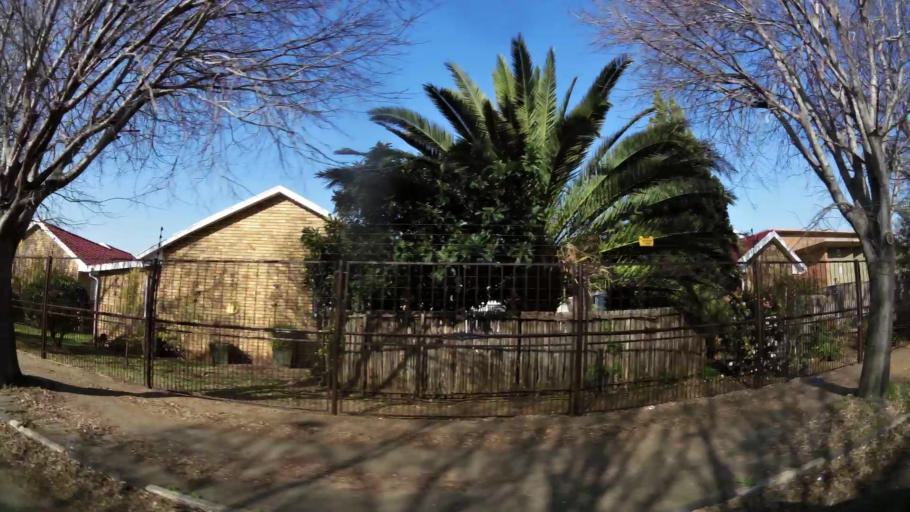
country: ZA
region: Gauteng
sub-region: West Rand District Municipality
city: Randfontein
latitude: -26.1774
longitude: 27.7069
